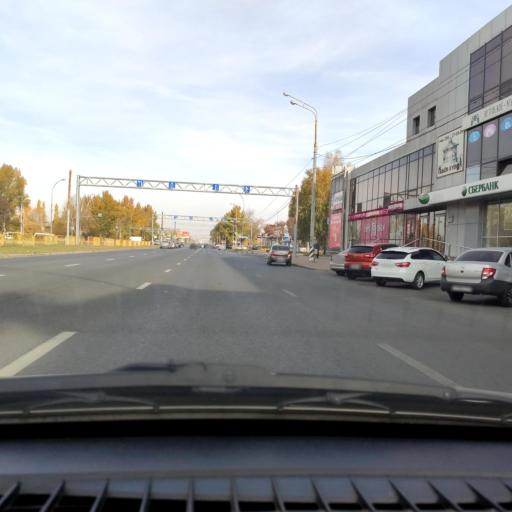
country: RU
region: Samara
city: Tol'yatti
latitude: 53.5360
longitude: 49.2836
